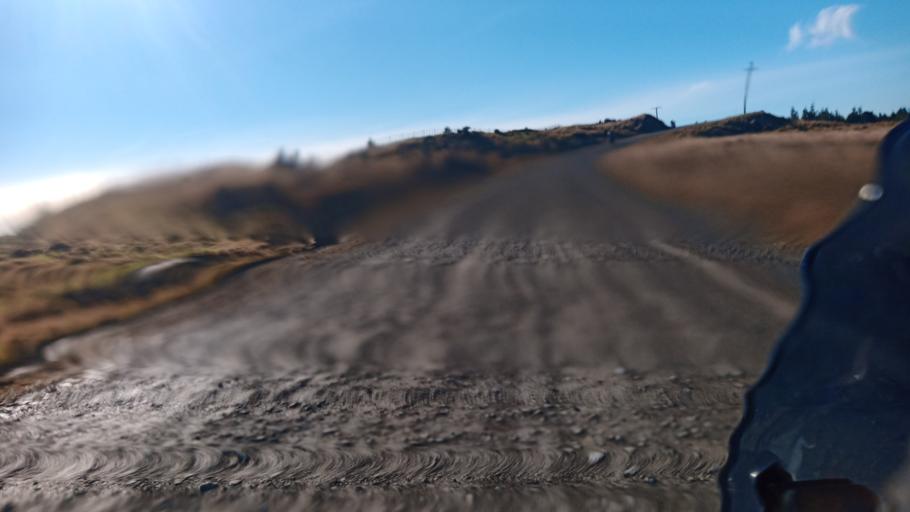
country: NZ
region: Gisborne
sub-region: Gisborne District
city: Gisborne
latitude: -38.1932
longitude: 177.8130
